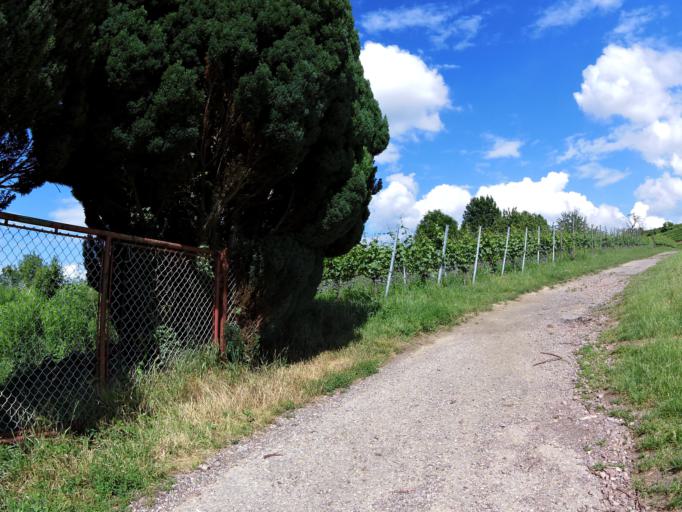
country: DE
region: Baden-Wuerttemberg
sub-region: Freiburg Region
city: Lahr
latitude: 48.3488
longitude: 7.8488
